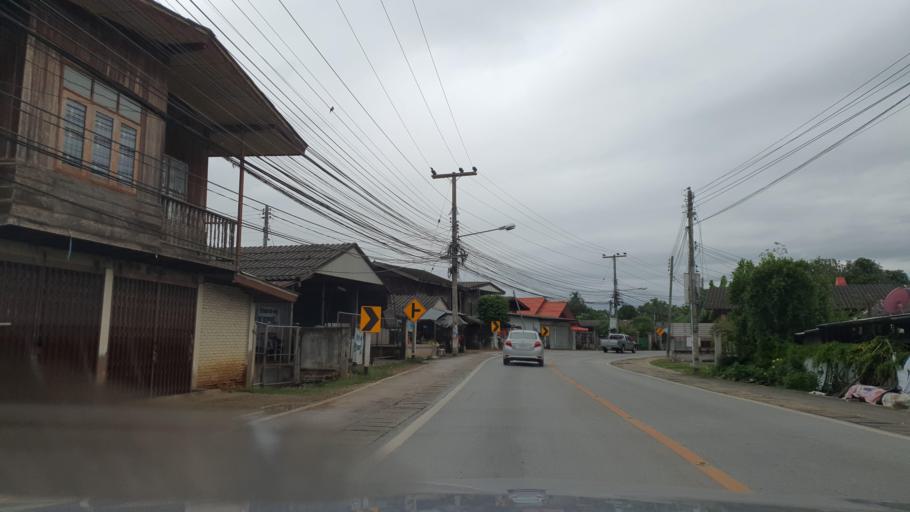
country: TH
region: Chiang Mai
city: San Pa Tong
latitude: 18.6238
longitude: 98.9334
